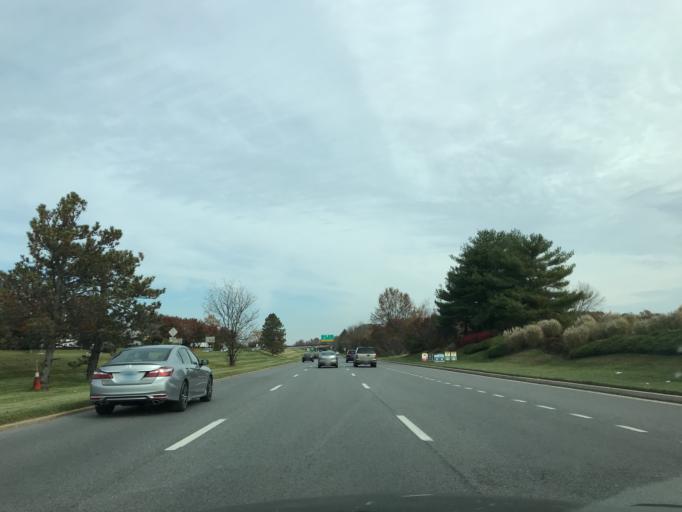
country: US
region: Maryland
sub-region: Howard County
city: Savage
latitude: 39.1861
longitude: -76.8171
